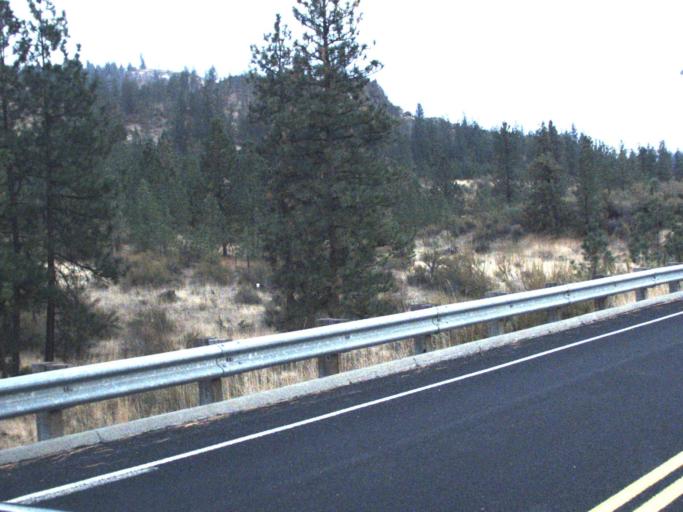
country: US
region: Washington
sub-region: Lincoln County
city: Davenport
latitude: 47.9033
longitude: -118.2748
